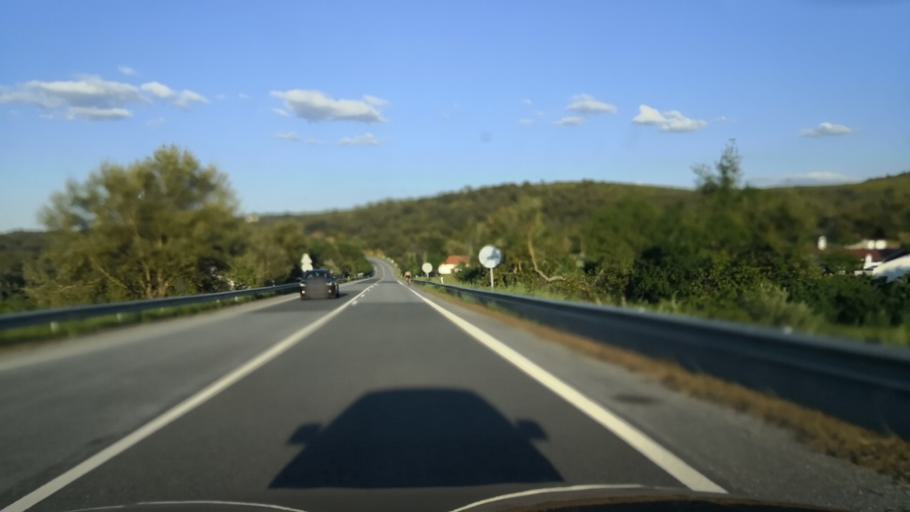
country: PT
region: Portalegre
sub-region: Portalegre
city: Sao Juliao
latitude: 39.3636
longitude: -7.3321
